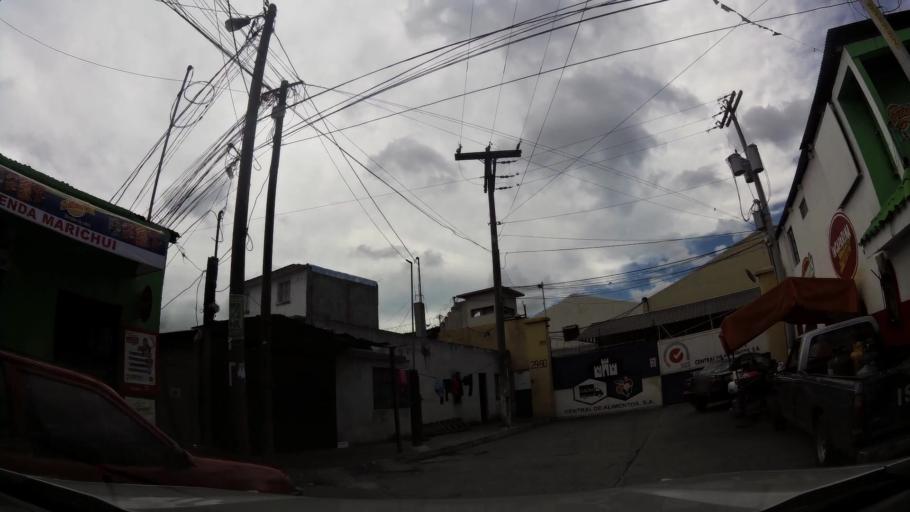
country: GT
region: Guatemala
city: Santa Catarina Pinula
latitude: 14.5958
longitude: -90.5362
